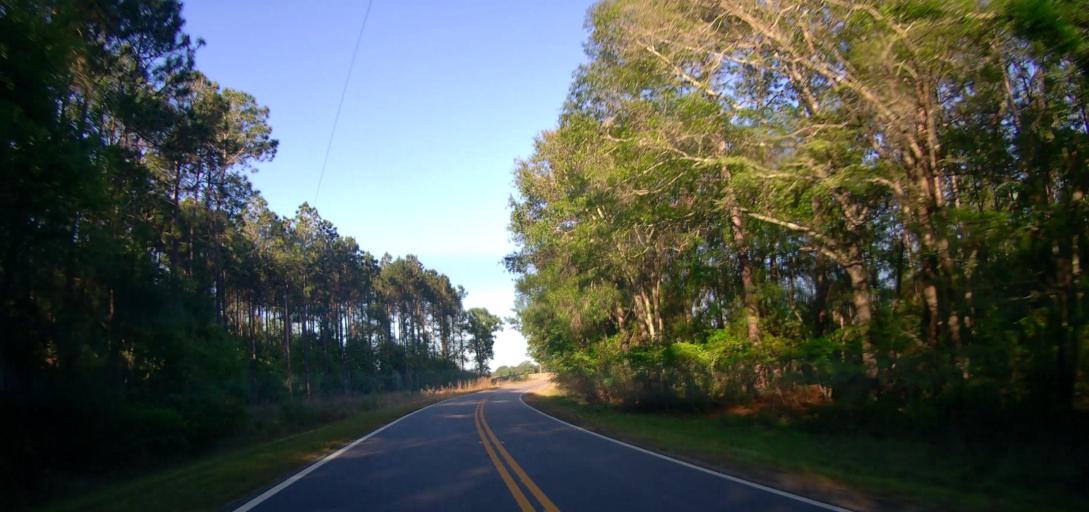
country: US
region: Georgia
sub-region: Ben Hill County
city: Fitzgerald
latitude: 31.6583
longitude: -83.1581
